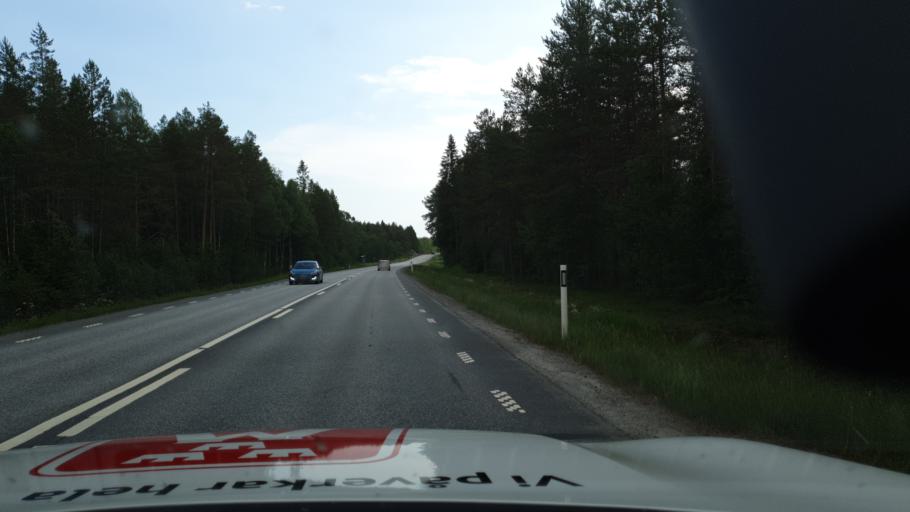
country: SE
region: Vaesterbotten
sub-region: Robertsfors Kommun
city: Robertsfors
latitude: 64.2635
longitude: 21.0464
